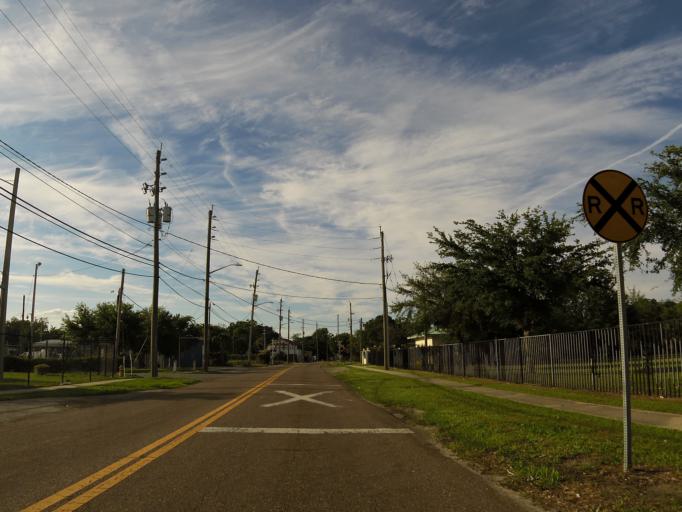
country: US
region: Florida
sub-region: Duval County
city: Jacksonville
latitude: 30.3518
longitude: -81.6584
